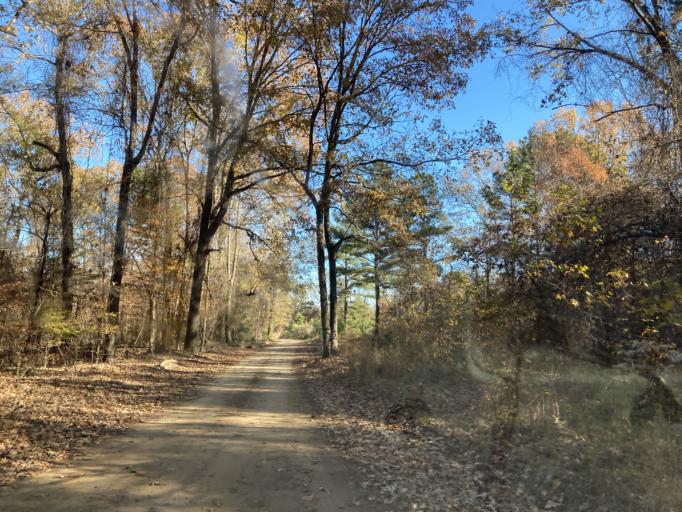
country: US
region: Mississippi
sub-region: Madison County
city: Kearney Park
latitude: 32.6709
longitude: -90.4493
